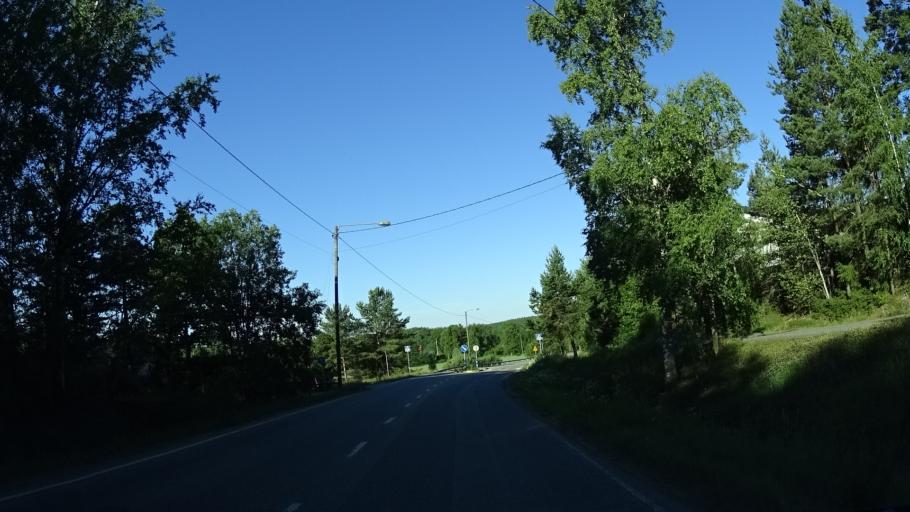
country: FI
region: Varsinais-Suomi
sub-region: Turku
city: Merimasku
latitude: 60.4586
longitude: 21.9014
